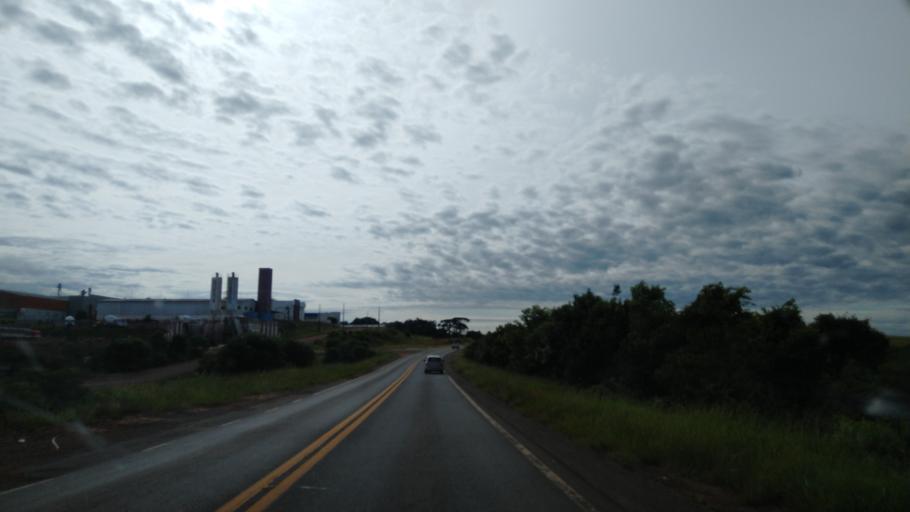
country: AR
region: Misiones
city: Bernardo de Irigoyen
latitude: -26.2601
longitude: -53.6136
